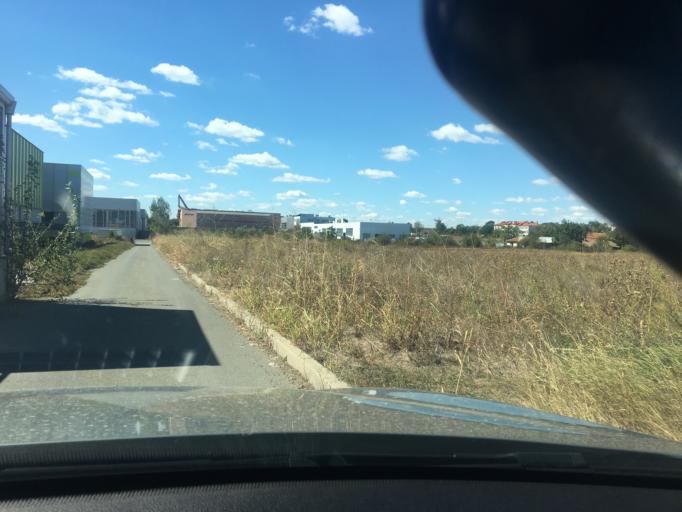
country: BG
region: Burgas
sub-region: Obshtina Burgas
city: Burgas
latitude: 42.5354
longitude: 27.4516
